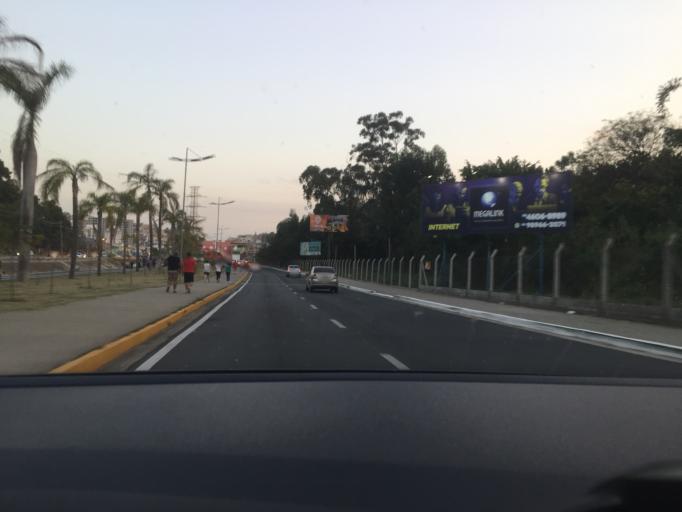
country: BR
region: Sao Paulo
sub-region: Varzea Paulista
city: Varzea Paulista
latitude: -23.2150
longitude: -46.8403
